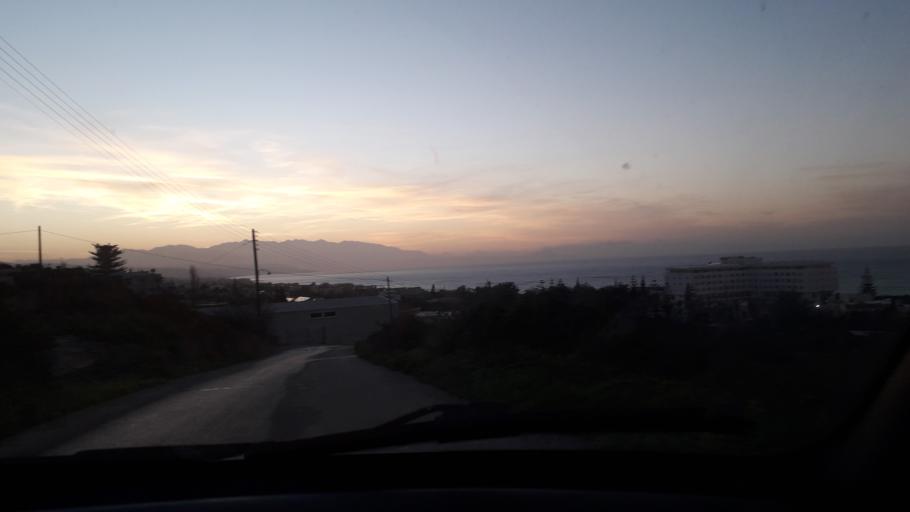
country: GR
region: Crete
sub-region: Nomos Rethymnis
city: Panormos
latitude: 35.3882
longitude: 24.6107
